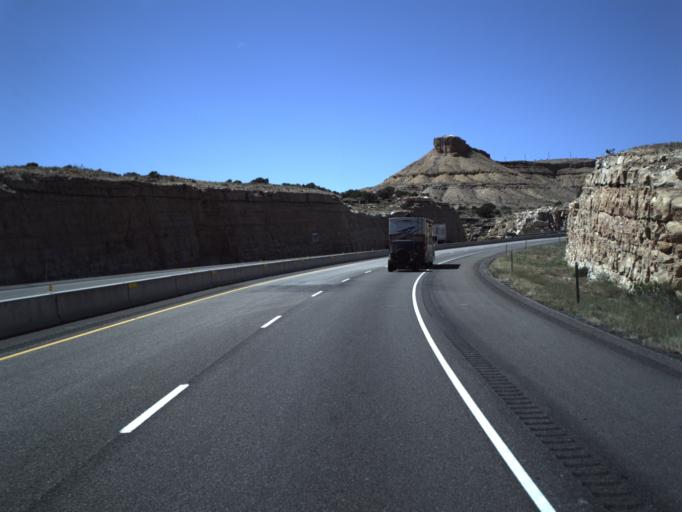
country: US
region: Utah
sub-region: Carbon County
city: East Carbon City
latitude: 38.9286
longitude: -110.4620
